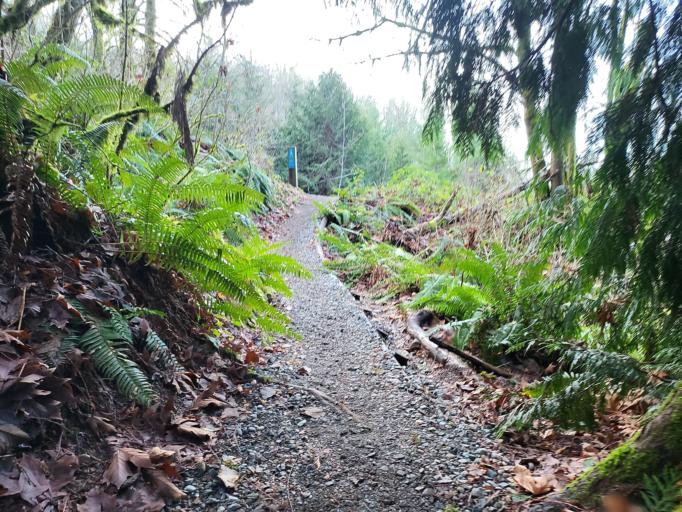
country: US
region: Washington
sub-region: King County
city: Newcastle
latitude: 47.5405
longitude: -122.1402
